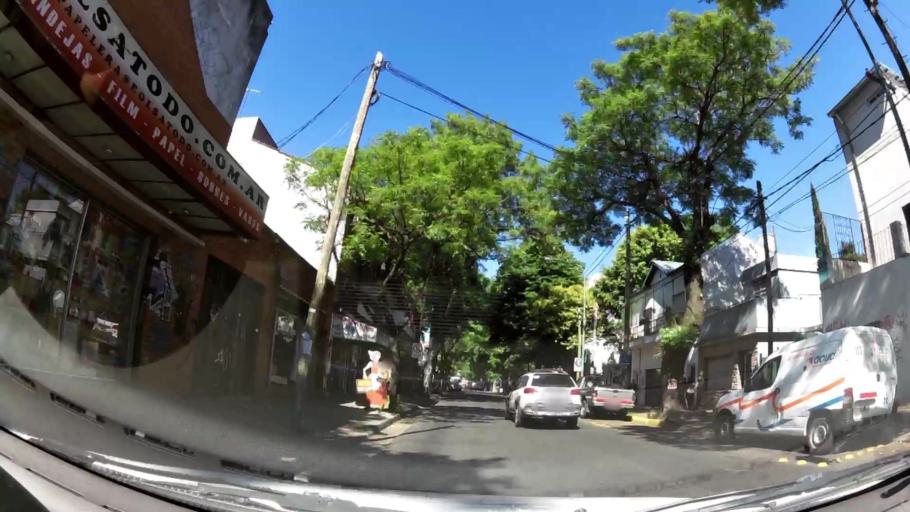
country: AR
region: Buenos Aires
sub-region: Partido de Vicente Lopez
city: Olivos
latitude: -34.5222
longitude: -58.4879
